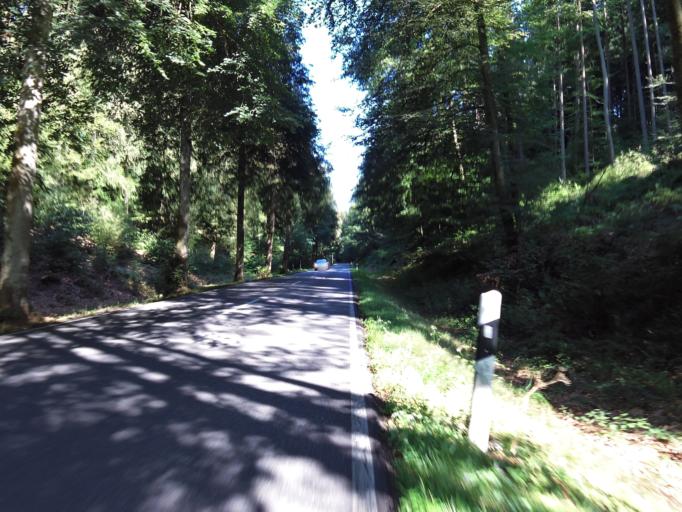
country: DE
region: Rheinland-Pfalz
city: Esthal
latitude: 49.3843
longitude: 7.9994
